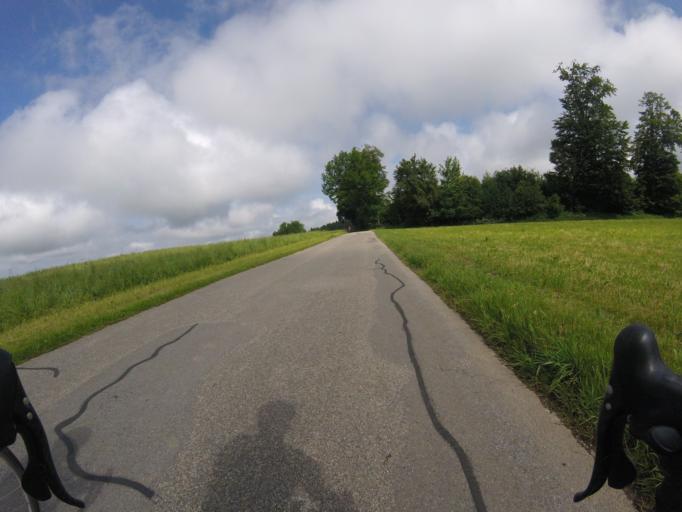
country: CH
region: Bern
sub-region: Bern-Mittelland District
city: Walkringen
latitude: 46.9591
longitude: 7.6002
